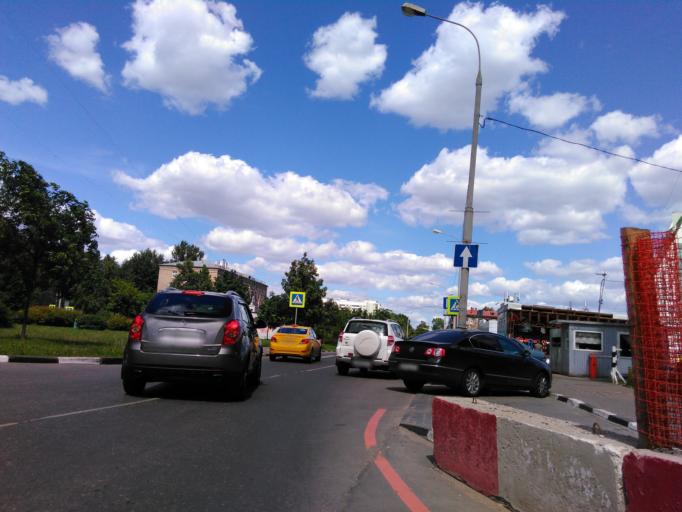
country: RU
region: Moscow
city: Novyye Cheremushki
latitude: 55.6828
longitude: 37.5808
